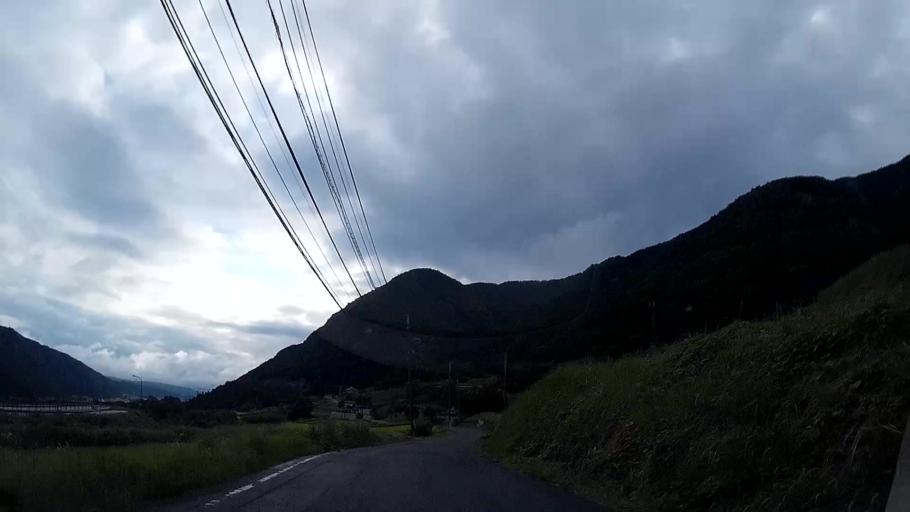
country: JP
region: Kumamoto
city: Ozu
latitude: 32.8797
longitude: 130.9634
